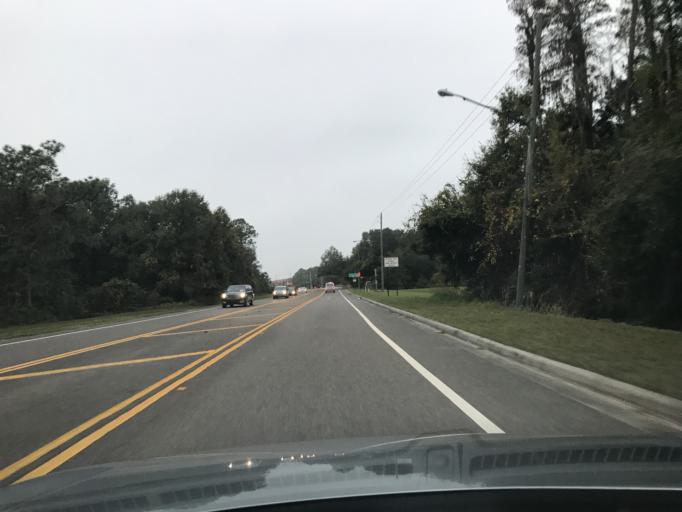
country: US
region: Florida
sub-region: Pinellas County
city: Oldsmar
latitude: 28.0558
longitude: -82.6442
